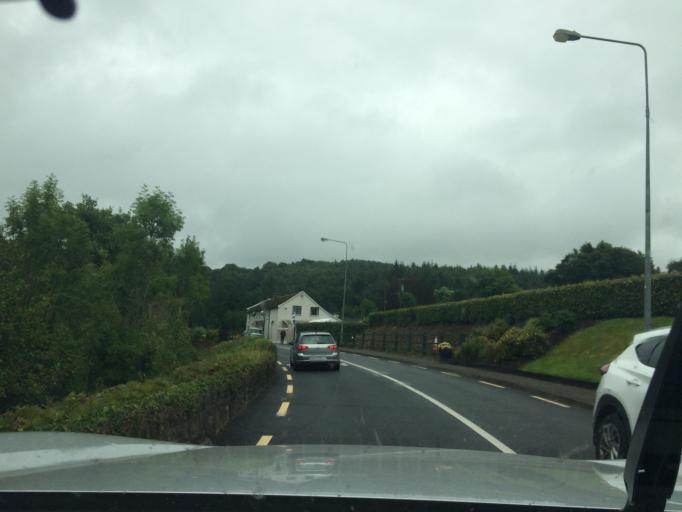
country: IE
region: Munster
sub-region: South Tipperary
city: Cluain Meala
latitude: 52.2667
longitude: -7.7126
